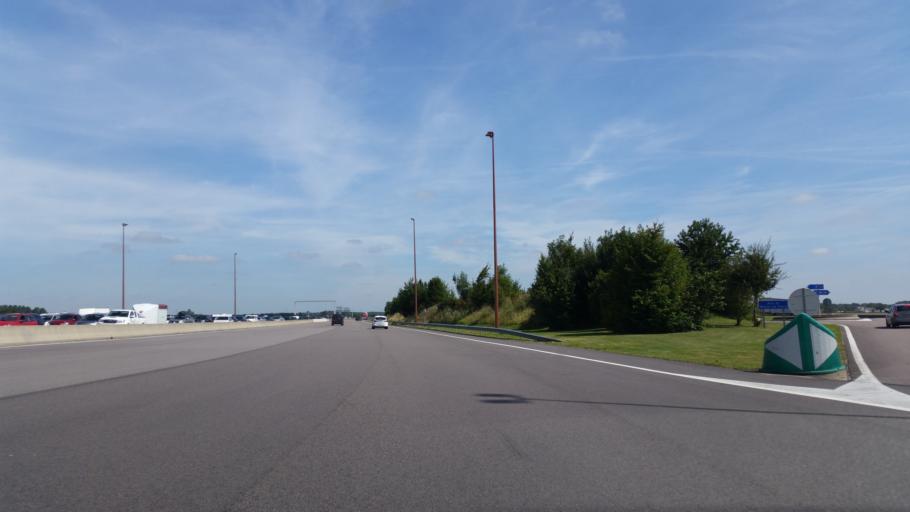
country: FR
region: Haute-Normandie
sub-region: Departement de la Seine-Maritime
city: Aumale
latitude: 49.7599
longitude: 1.7036
